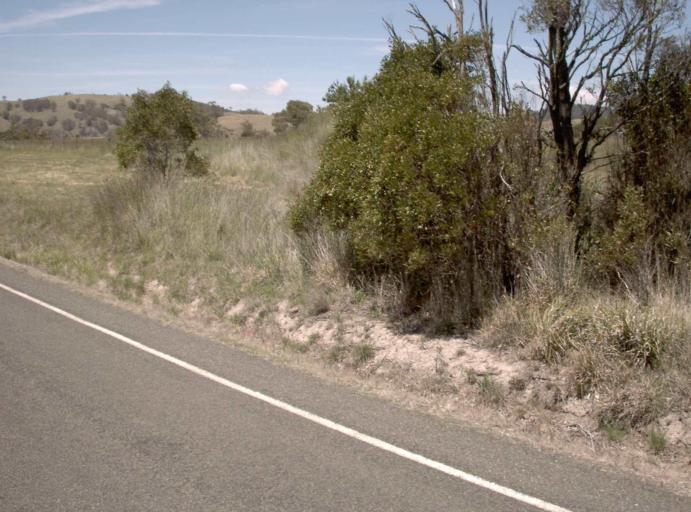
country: AU
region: Victoria
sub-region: Alpine
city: Mount Beauty
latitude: -37.1519
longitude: 147.6512
